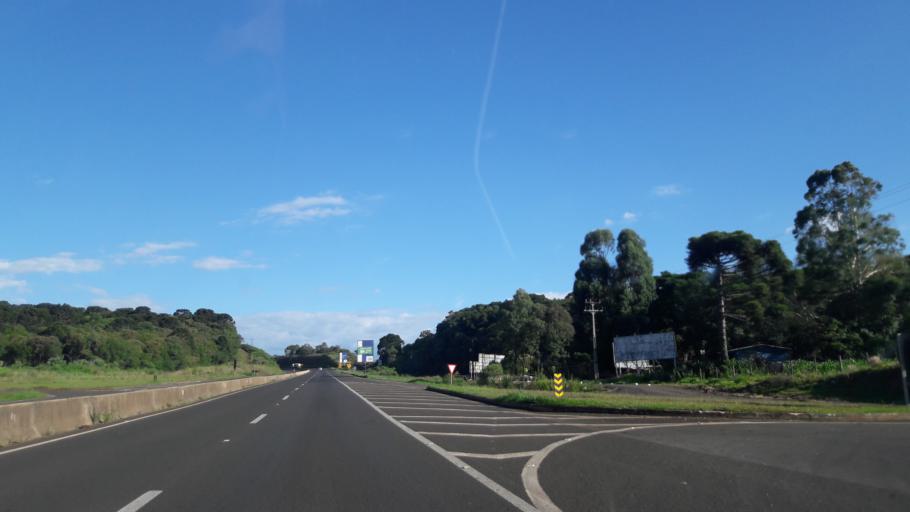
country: BR
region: Parana
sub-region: Guarapuava
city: Guarapuava
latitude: -25.3428
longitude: -51.4115
